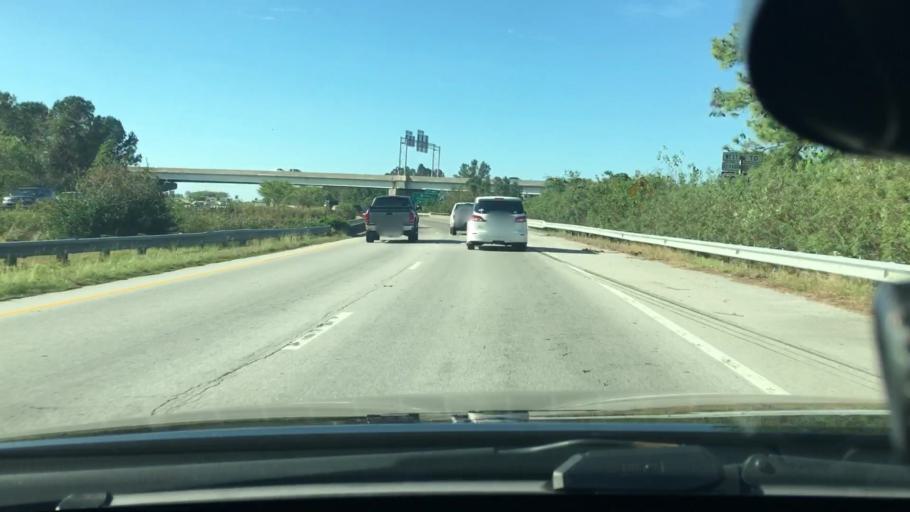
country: US
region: North Carolina
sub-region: Craven County
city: James City
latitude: 35.0926
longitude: -77.0376
